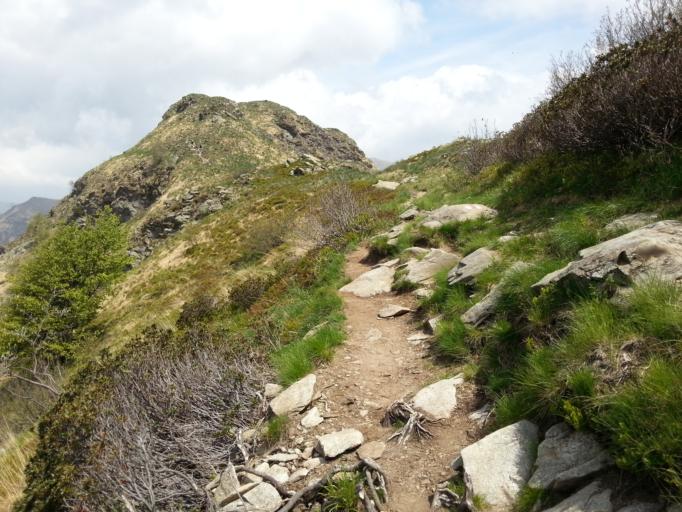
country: IT
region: Lombardy
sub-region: Provincia di Varese
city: Curiglia
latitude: 46.0557
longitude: 8.8554
